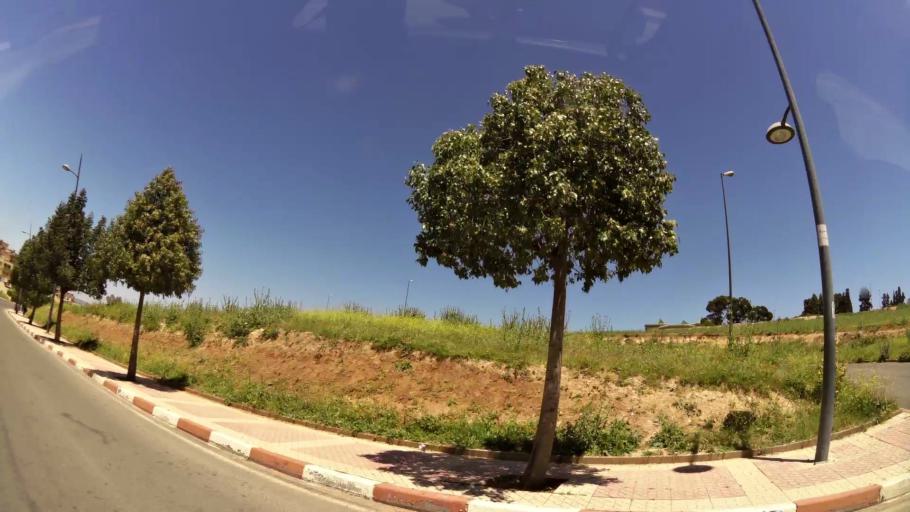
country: MA
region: Meknes-Tafilalet
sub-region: Meknes
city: Meknes
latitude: 33.9055
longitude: -5.5561
